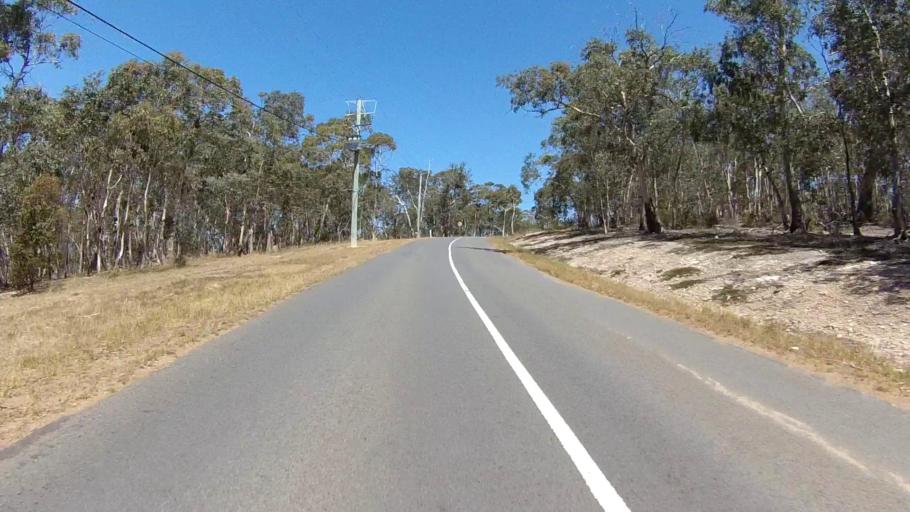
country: AU
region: Tasmania
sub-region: Clarence
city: Sandford
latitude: -42.9962
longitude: 147.4770
